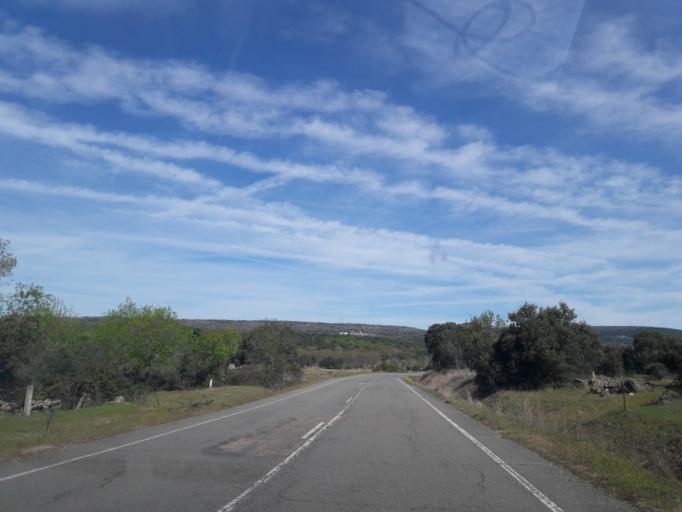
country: ES
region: Castille and Leon
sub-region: Provincia de Salamanca
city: Ledrada
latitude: 40.4811
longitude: -5.7268
